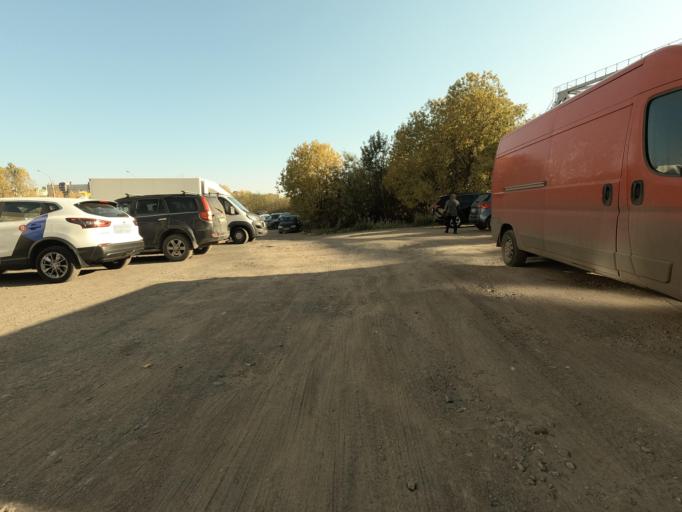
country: RU
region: Leningrad
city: Rybatskoye
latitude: 59.8411
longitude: 30.4770
